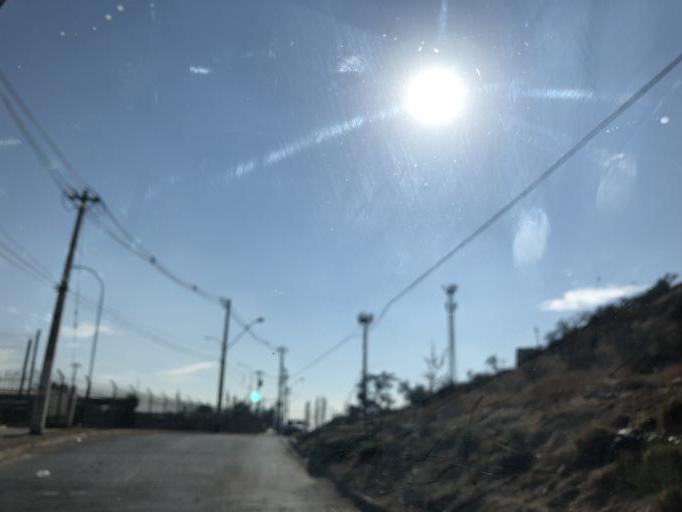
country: CL
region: Santiago Metropolitan
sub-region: Provincia de Cordillera
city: Puente Alto
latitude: -33.6181
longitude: -70.6033
